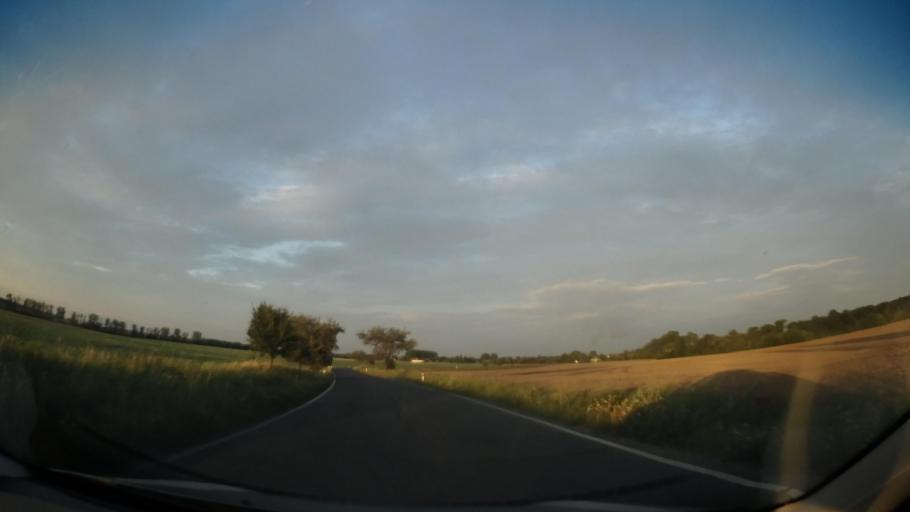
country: CZ
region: Central Bohemia
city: Milovice
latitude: 50.2265
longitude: 14.9270
